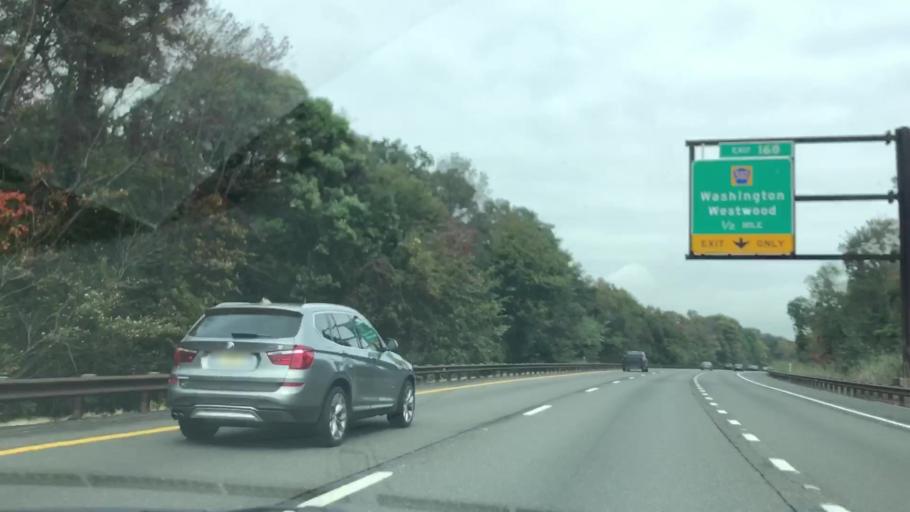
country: US
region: New Jersey
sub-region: Bergen County
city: Ho-Ho-Kus
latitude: 40.9900
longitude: -74.0729
